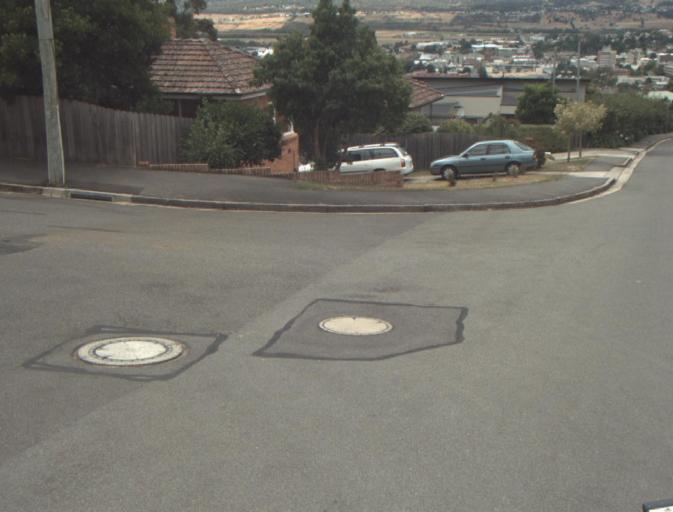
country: AU
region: Tasmania
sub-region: Launceston
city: Launceston
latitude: -41.4405
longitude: 147.1207
